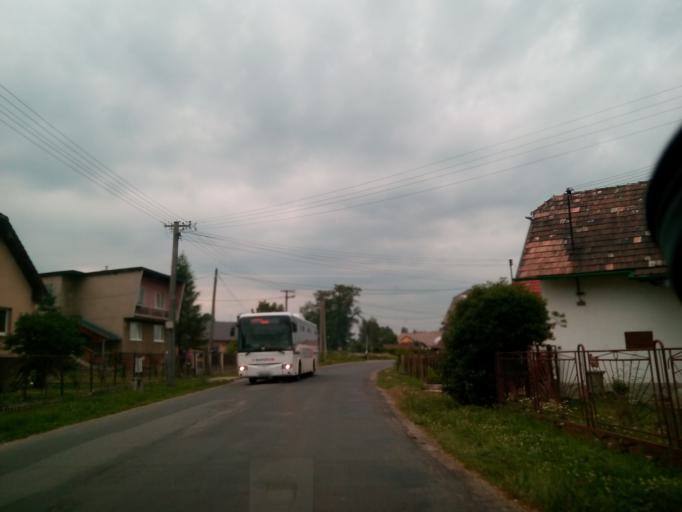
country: SK
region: Kosicky
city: Spisska Nova Ves
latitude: 48.9102
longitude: 20.6384
